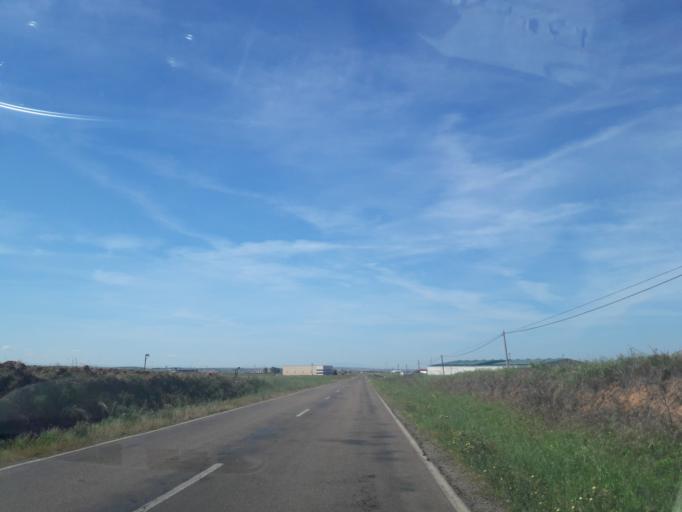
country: ES
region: Castille and Leon
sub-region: Provincia de Salamanca
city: Villoruela
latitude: 40.9929
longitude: -5.4037
